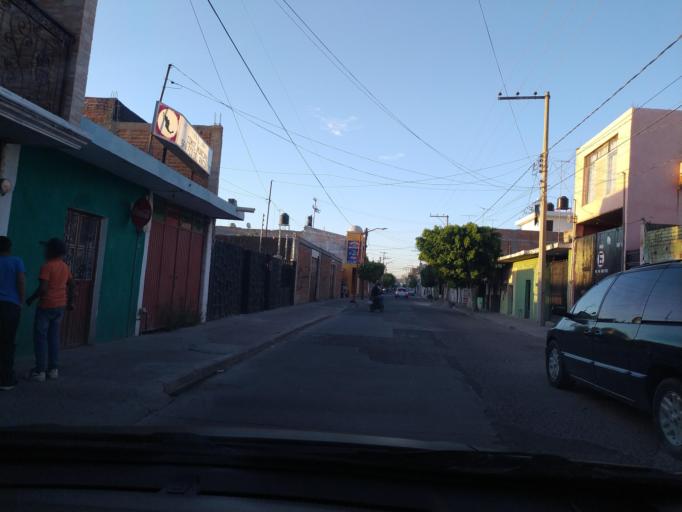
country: MX
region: Guanajuato
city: San Francisco del Rincon
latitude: 21.0124
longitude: -101.8542
